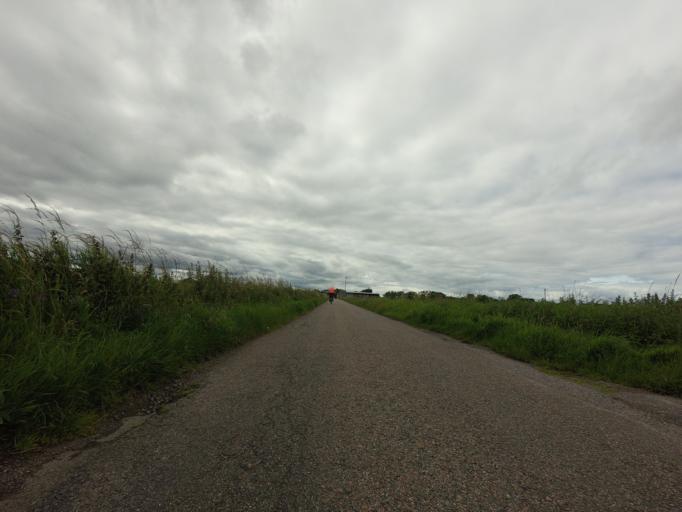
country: GB
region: Scotland
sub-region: Moray
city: Forres
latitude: 57.6272
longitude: -3.6039
